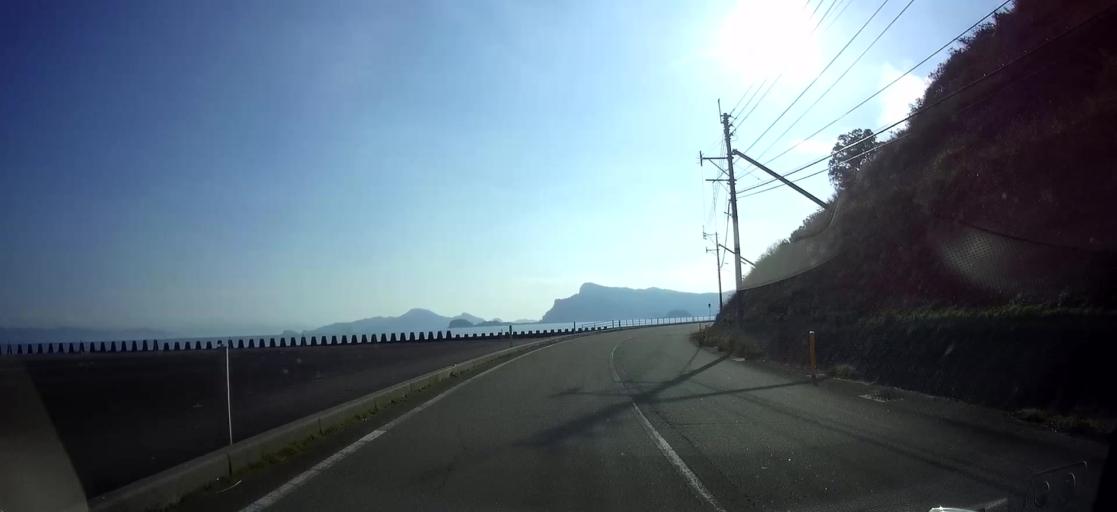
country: JP
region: Kumamoto
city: Yatsushiro
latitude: 32.4555
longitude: 130.4285
